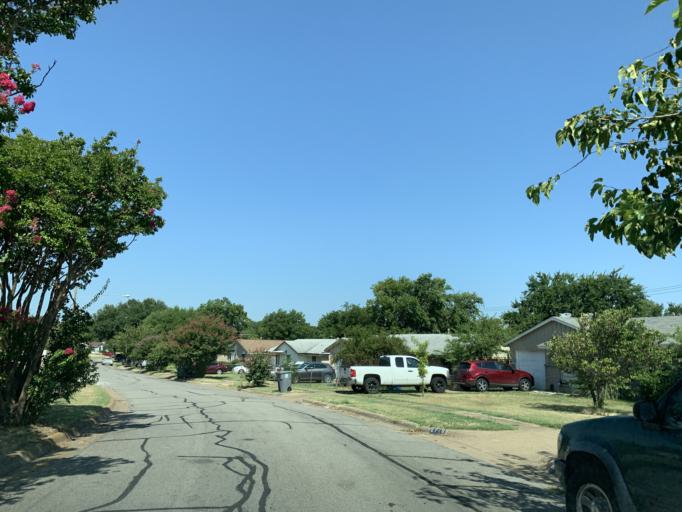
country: US
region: Texas
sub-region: Dallas County
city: Hutchins
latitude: 32.6623
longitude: -96.7547
